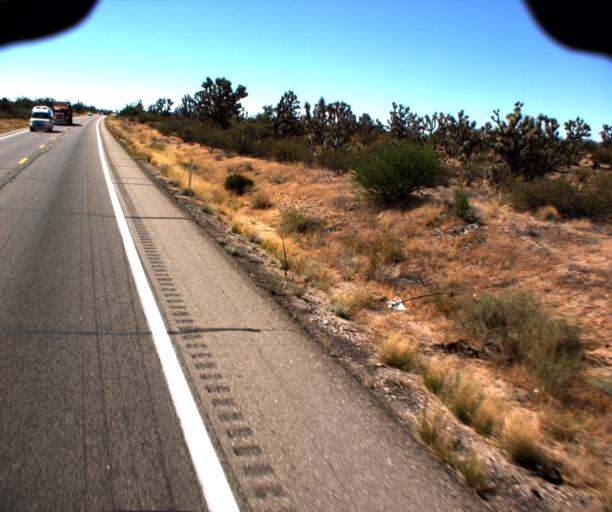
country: US
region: Arizona
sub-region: Yavapai County
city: Congress
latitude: 34.2711
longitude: -113.0948
